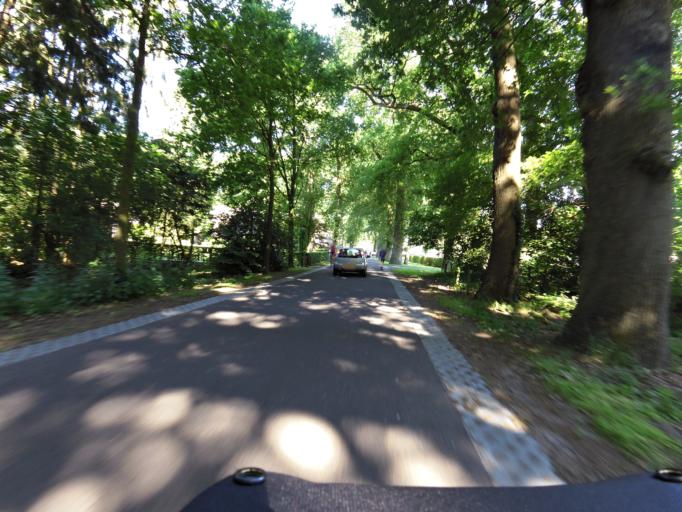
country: NL
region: Overijssel
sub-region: Gemeente Dalfsen
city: Dalfsen
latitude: 52.5100
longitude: 6.3534
